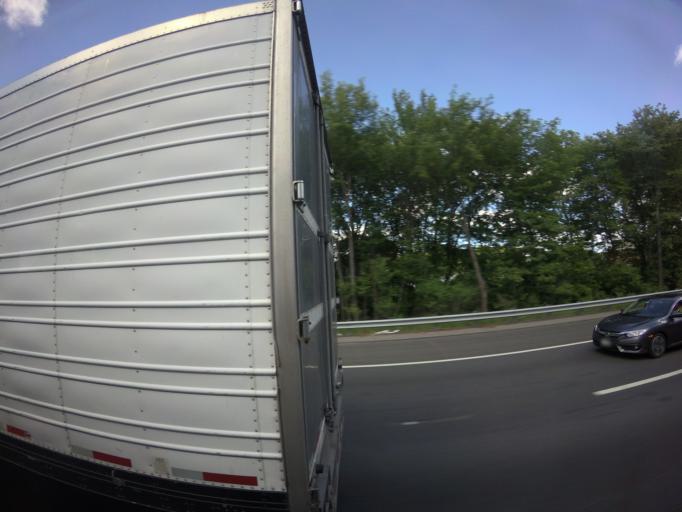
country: US
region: Massachusetts
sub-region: Middlesex County
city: Wilmington
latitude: 42.5906
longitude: -71.1645
